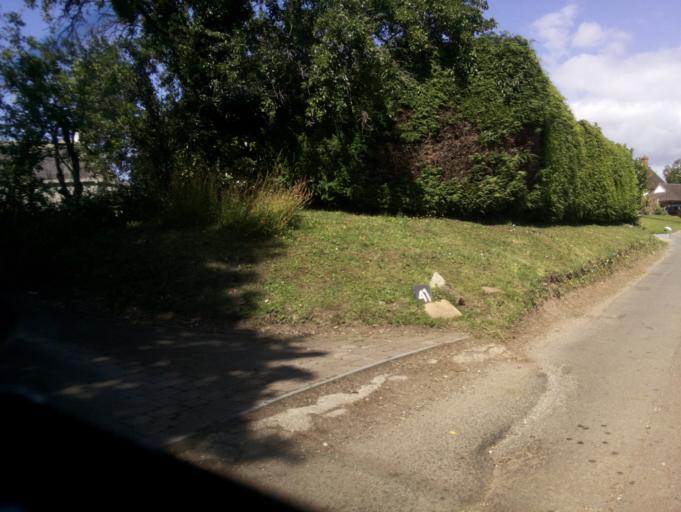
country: GB
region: England
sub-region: Milton Keynes
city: Calverton
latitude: 52.0014
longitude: -0.8633
